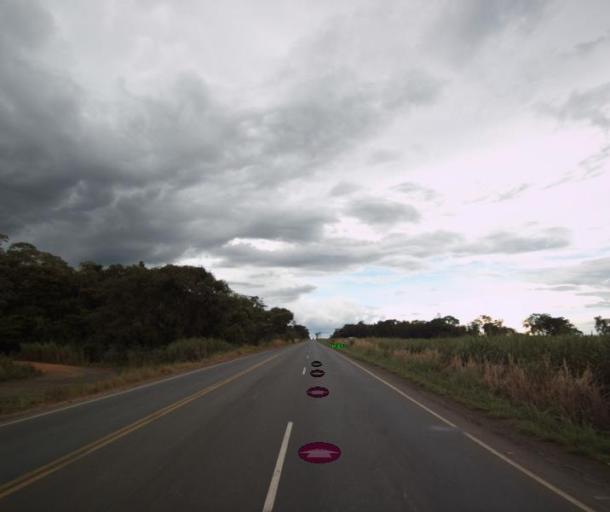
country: BR
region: Goias
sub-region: Itapaci
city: Itapaci
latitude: -14.9963
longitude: -49.4085
